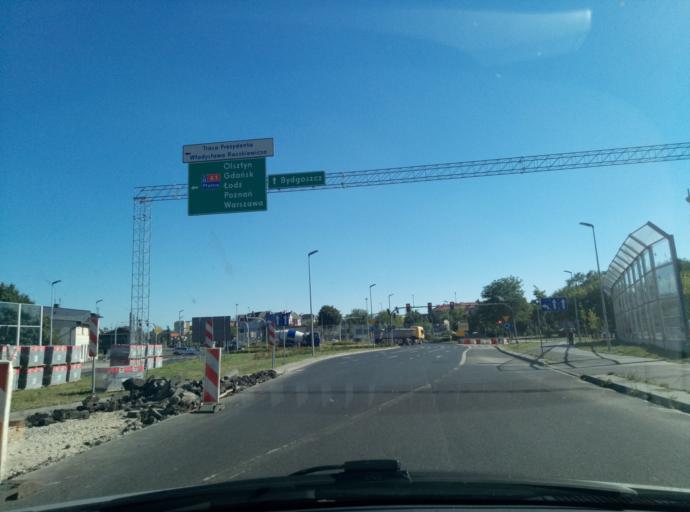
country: PL
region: Kujawsko-Pomorskie
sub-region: Torun
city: Torun
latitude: 53.0259
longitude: 18.5913
